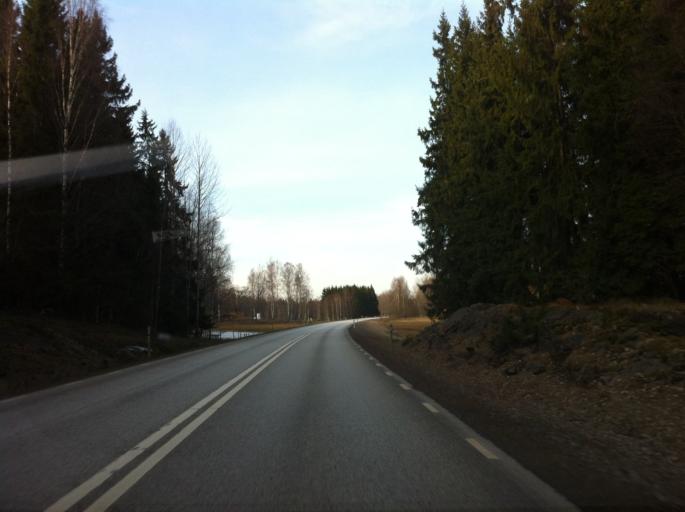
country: SE
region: Vaermland
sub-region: Storfors Kommun
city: Storfors
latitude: 59.5765
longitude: 14.2578
